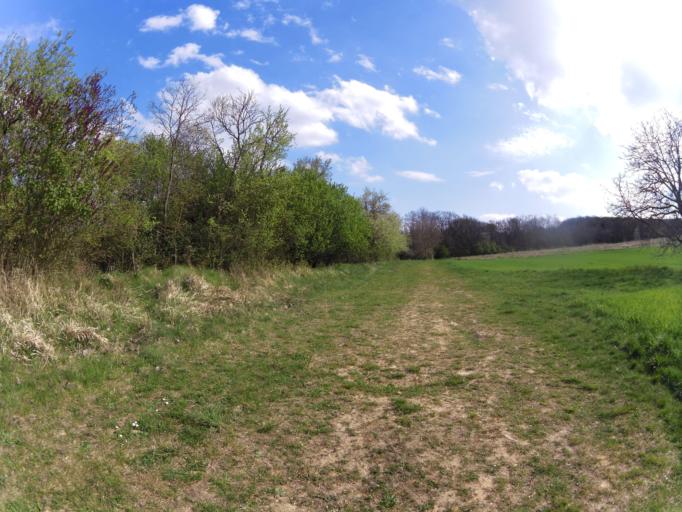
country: DE
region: Bavaria
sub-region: Regierungsbezirk Unterfranken
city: Winterhausen
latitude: 49.6994
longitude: 10.0172
